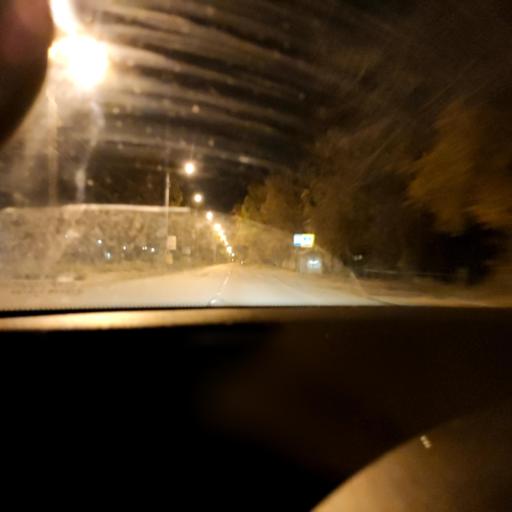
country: RU
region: Samara
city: Petra-Dubrava
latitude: 53.2373
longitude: 50.3075
